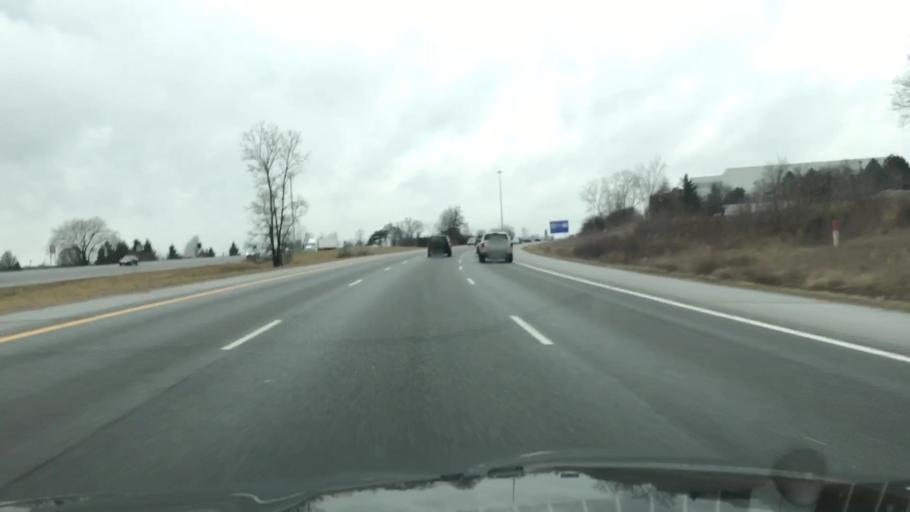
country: US
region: Michigan
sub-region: Oakland County
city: Auburn Hills
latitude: 42.6960
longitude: -83.2672
